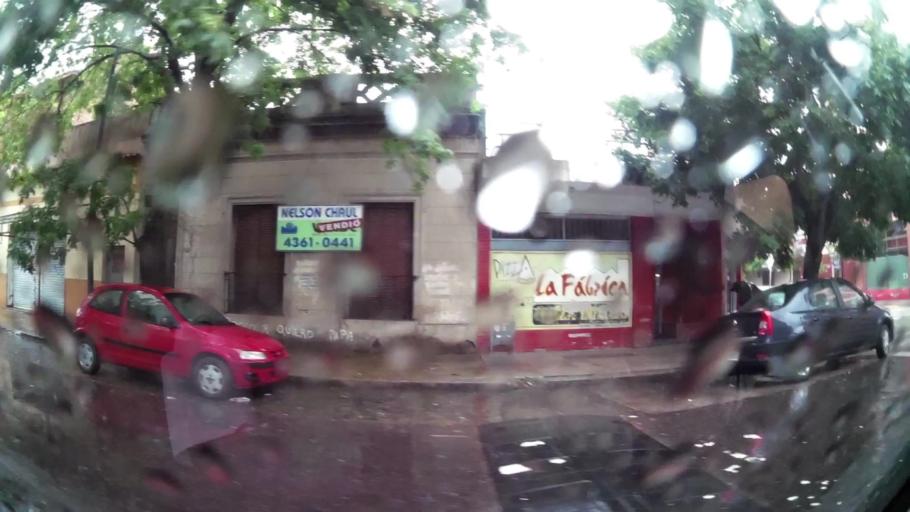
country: AR
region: Buenos Aires F.D.
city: Buenos Aires
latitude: -34.6329
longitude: -58.3725
